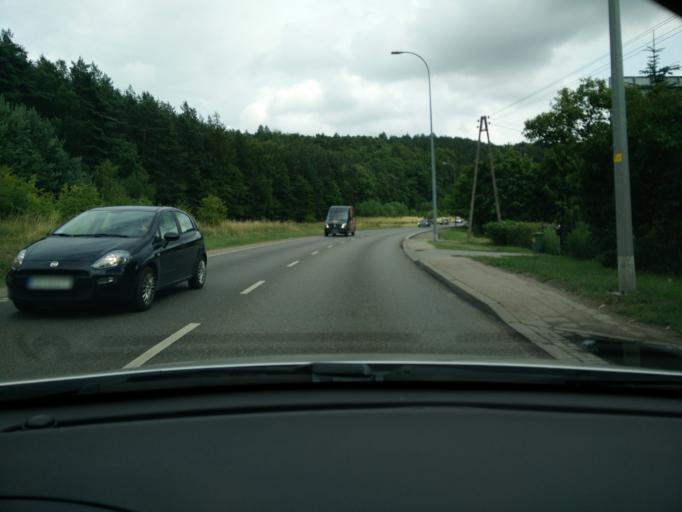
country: PL
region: Pomeranian Voivodeship
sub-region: Sopot
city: Sopot
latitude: 54.4213
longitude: 18.5386
